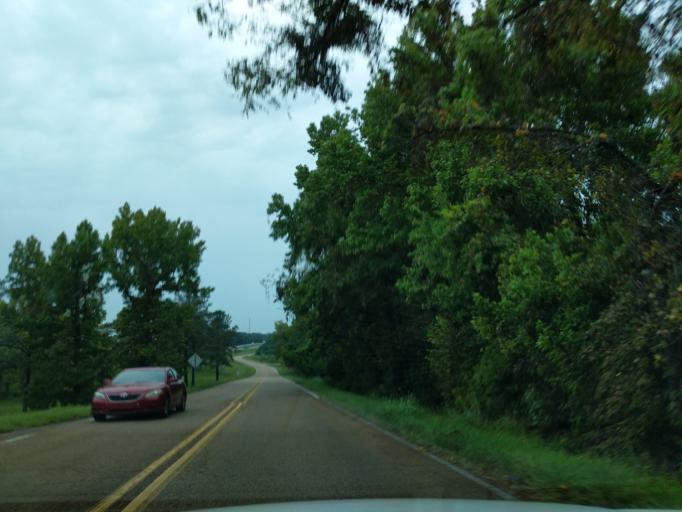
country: US
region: Mississippi
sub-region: Warren County
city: Vicksburg
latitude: 32.3214
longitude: -90.8781
